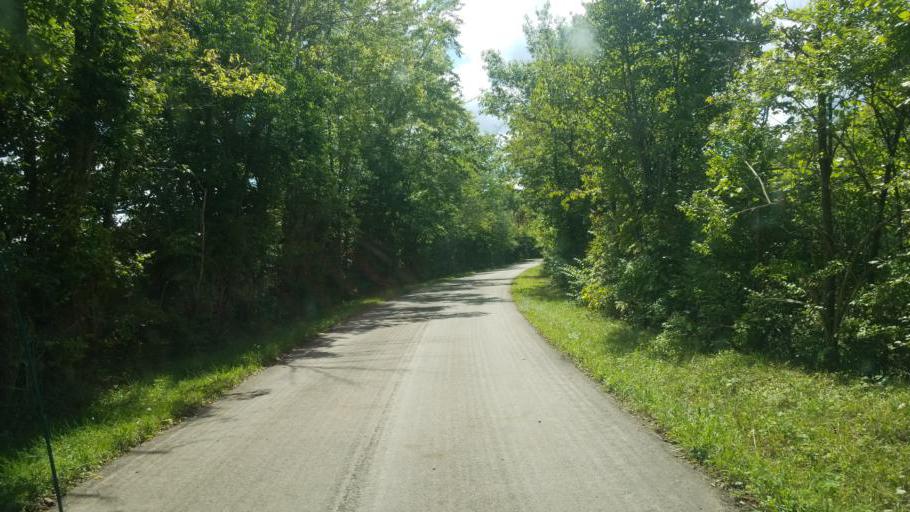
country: US
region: Ohio
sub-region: Marion County
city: Prospect
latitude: 40.4398
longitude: -83.1918
